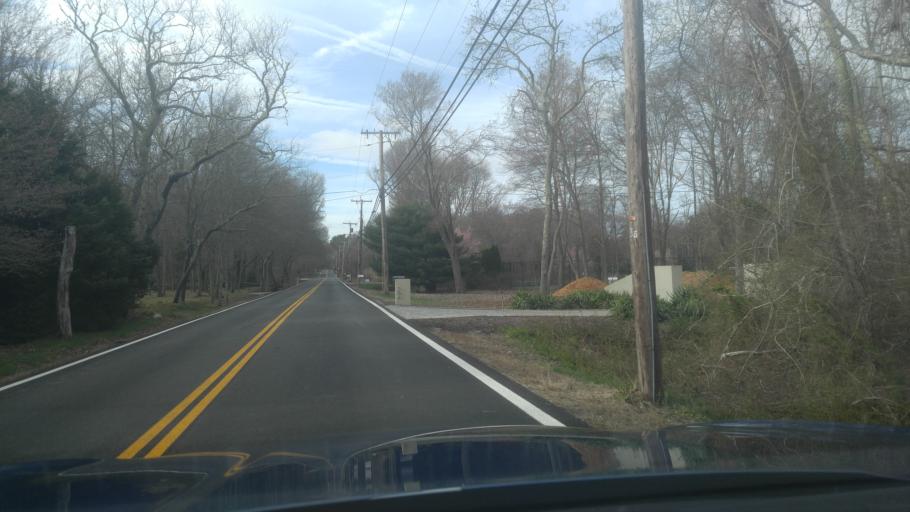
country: US
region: Rhode Island
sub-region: Newport County
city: Jamestown
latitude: 41.5509
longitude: -71.3630
